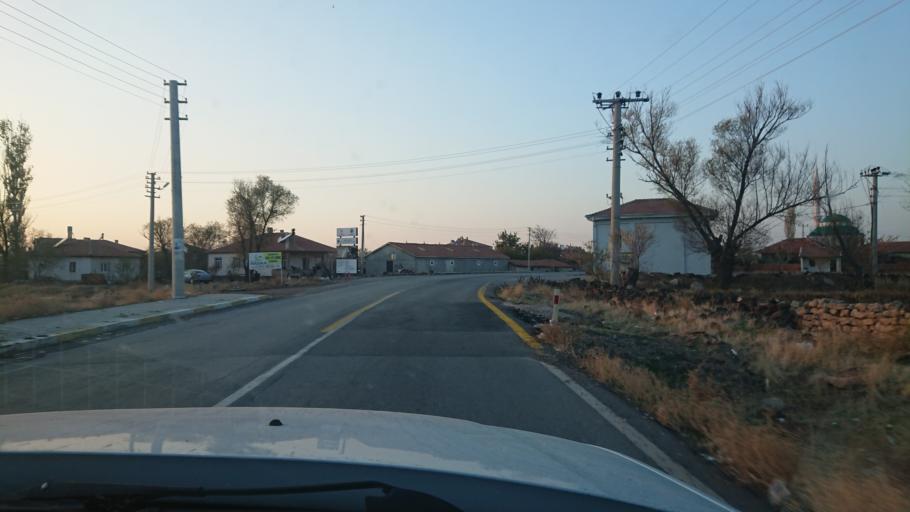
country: TR
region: Aksaray
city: Aksaray
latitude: 38.3169
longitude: 34.0538
